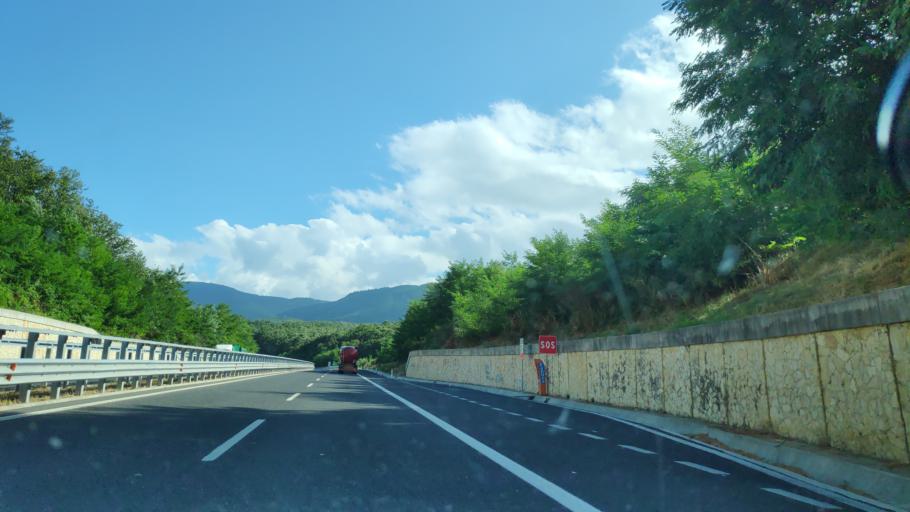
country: IT
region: Campania
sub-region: Provincia di Salerno
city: Casalbuono
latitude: 40.2430
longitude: 15.6596
